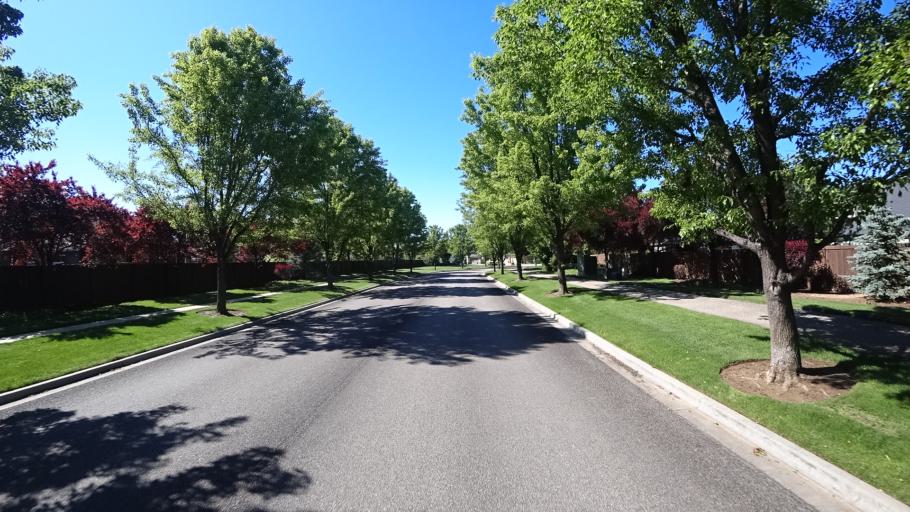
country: US
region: Idaho
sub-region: Ada County
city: Meridian
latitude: 43.6591
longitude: -116.4012
